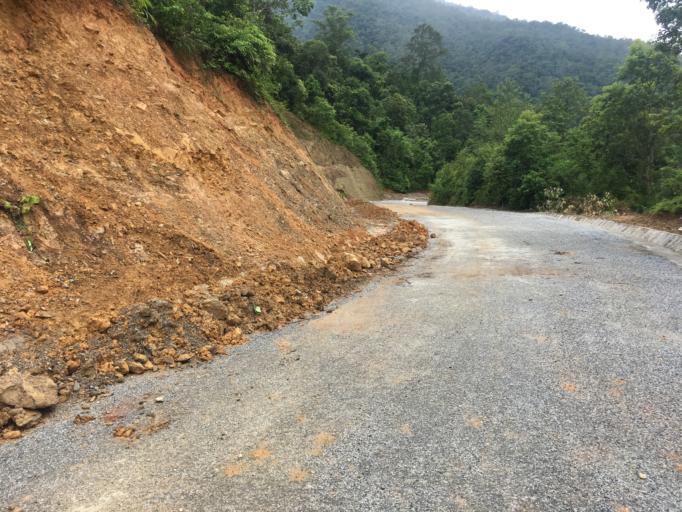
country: VN
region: Ha Giang
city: Thi Tran Tam Son
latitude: 22.9949
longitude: 105.0680
